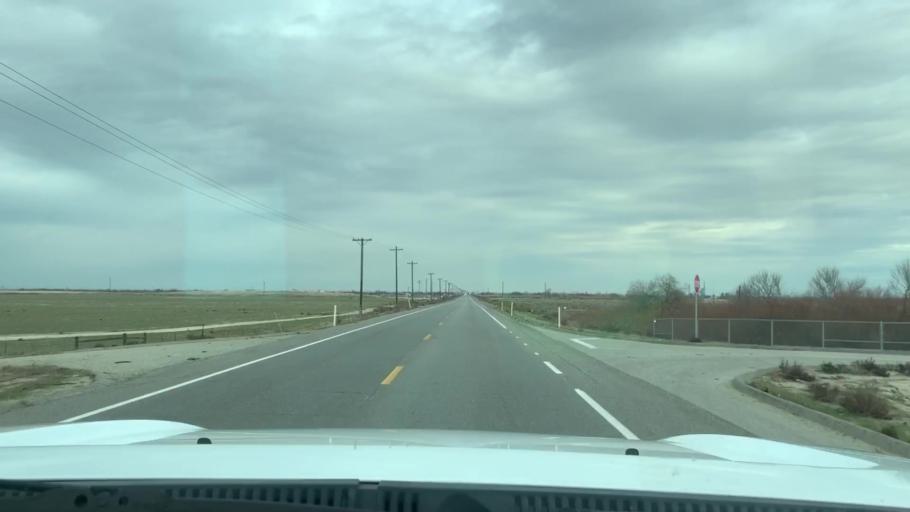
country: US
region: California
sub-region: Kern County
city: Rosedale
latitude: 35.3060
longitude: -119.2524
